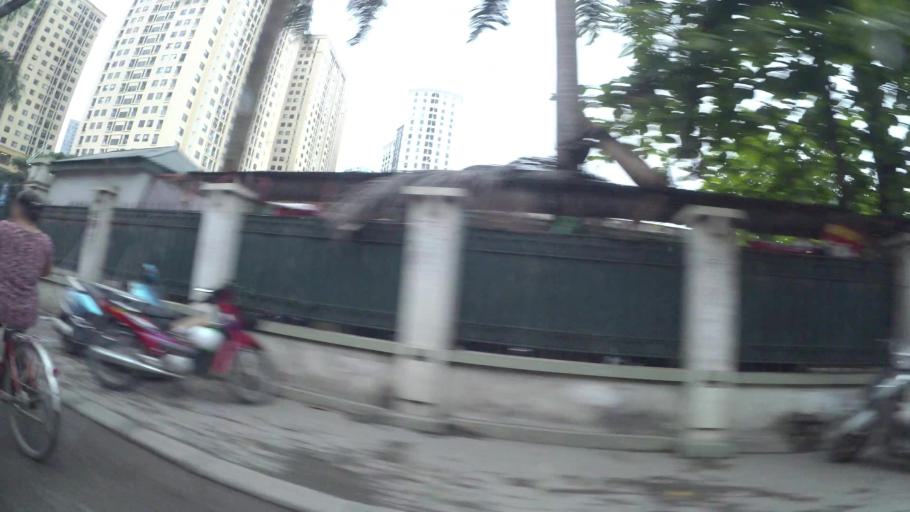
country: VN
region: Ha Noi
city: Hai BaTrung
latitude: 20.9881
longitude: 105.8668
